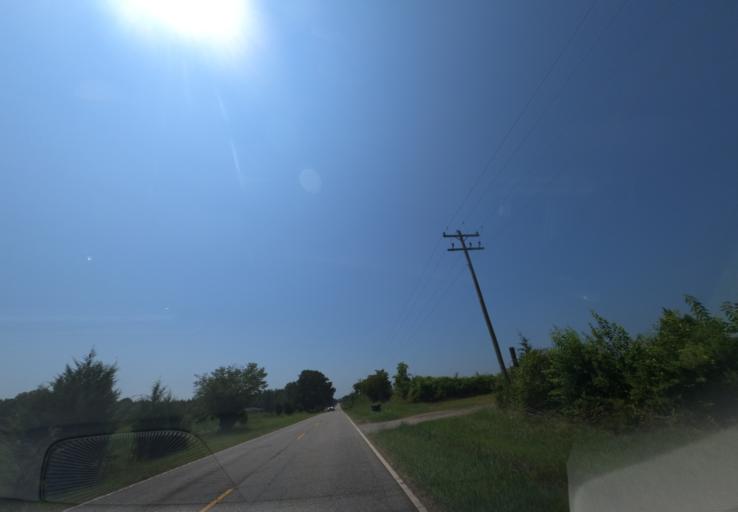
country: US
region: South Carolina
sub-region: Greenwood County
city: Greenwood
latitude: 34.0268
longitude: -82.1285
